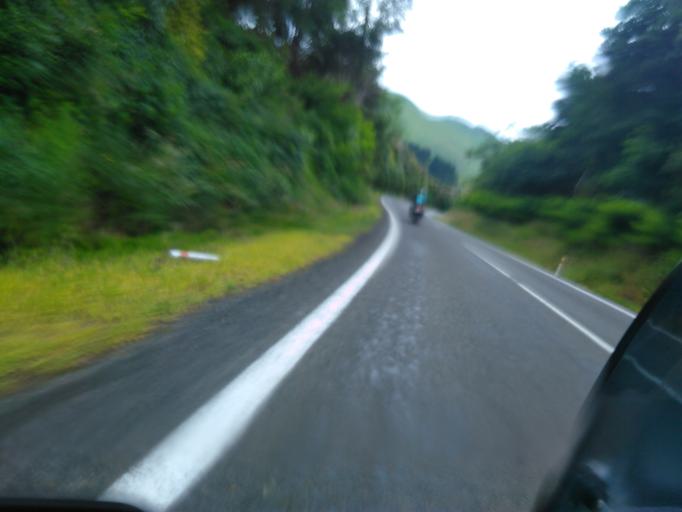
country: NZ
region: Gisborne
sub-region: Gisborne District
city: Gisborne
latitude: -38.4537
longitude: 177.6329
